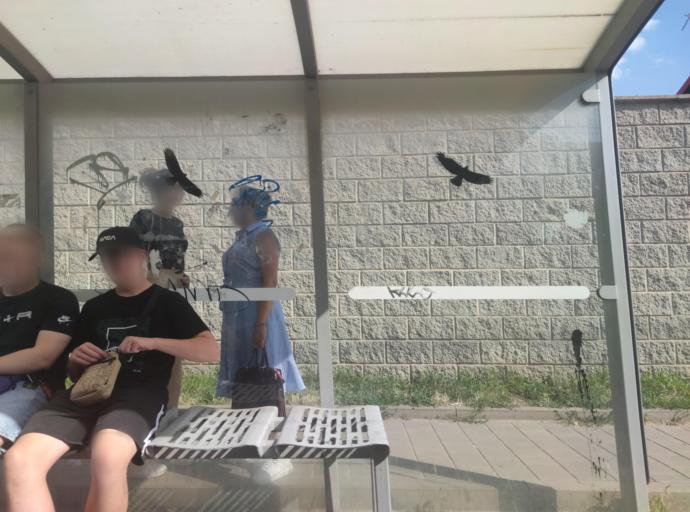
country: CZ
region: South Moravian
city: Podoli
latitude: 49.1762
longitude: 16.6873
